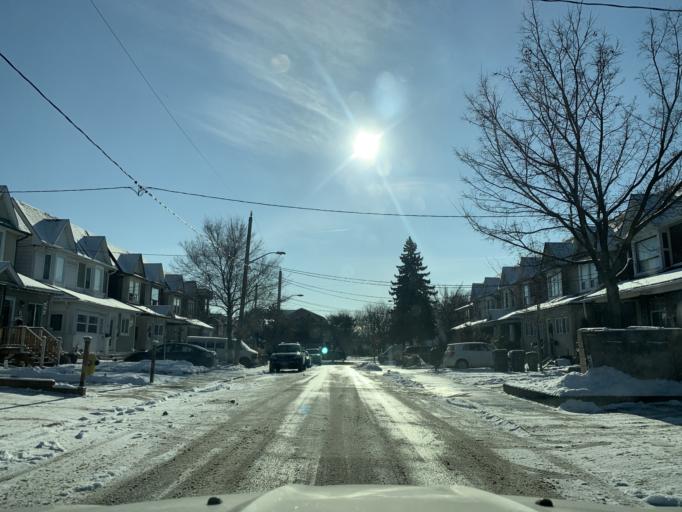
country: CA
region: Ontario
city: Toronto
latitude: 43.6721
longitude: -79.4811
